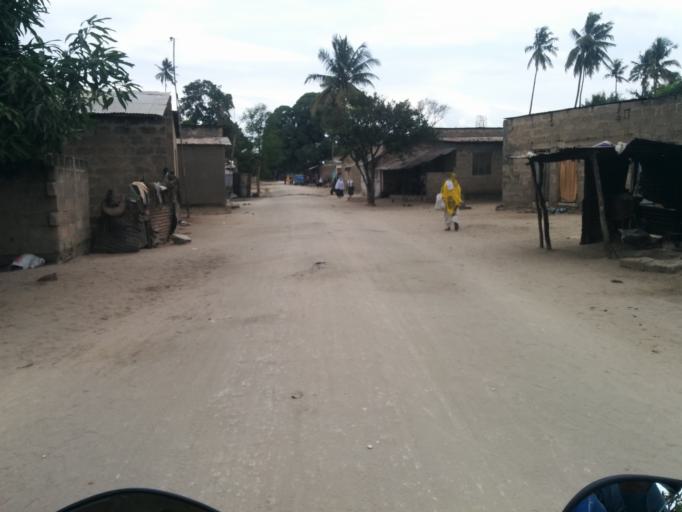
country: TZ
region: Dar es Salaam
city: Dar es Salaam
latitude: -6.8734
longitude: 39.2464
